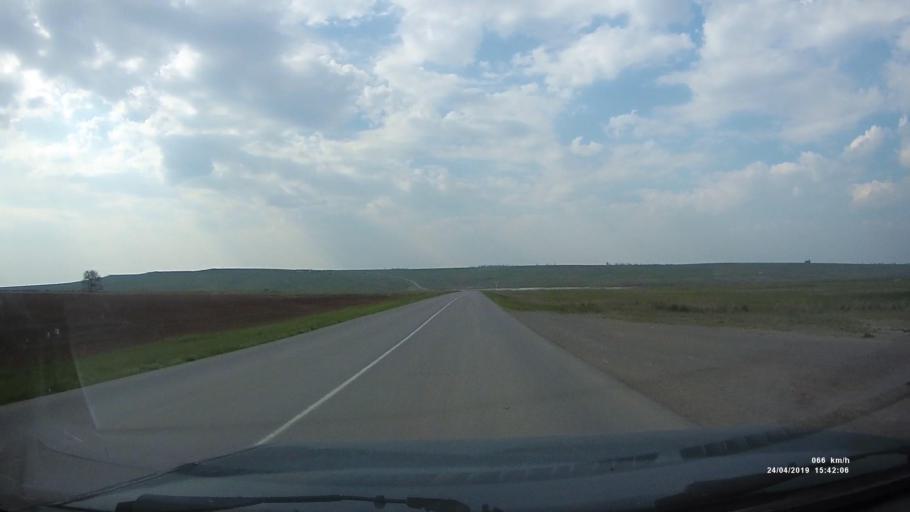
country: RU
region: Kalmykiya
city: Yashalta
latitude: 46.5732
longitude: 42.7916
